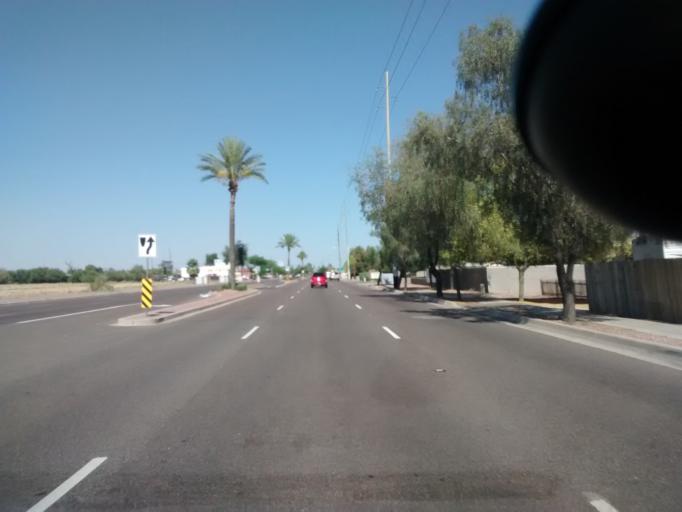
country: US
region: Arizona
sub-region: Maricopa County
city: Peoria
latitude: 33.5377
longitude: -112.2422
